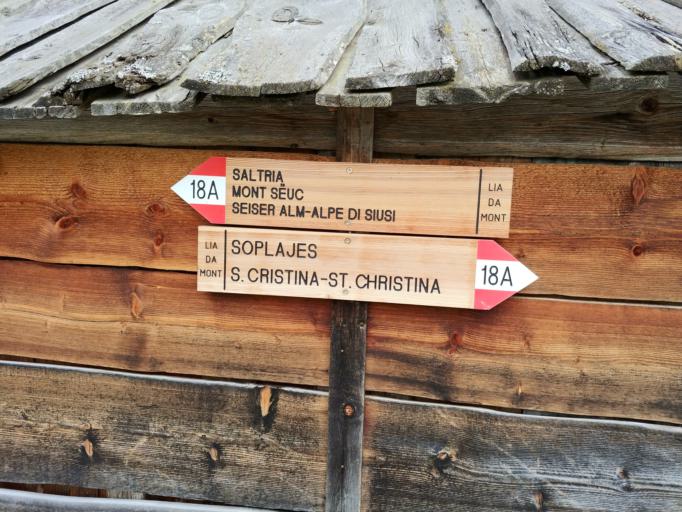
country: IT
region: Trentino-Alto Adige
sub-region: Bolzano
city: Santa Cristina Valgardena
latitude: 46.5568
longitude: 11.7036
